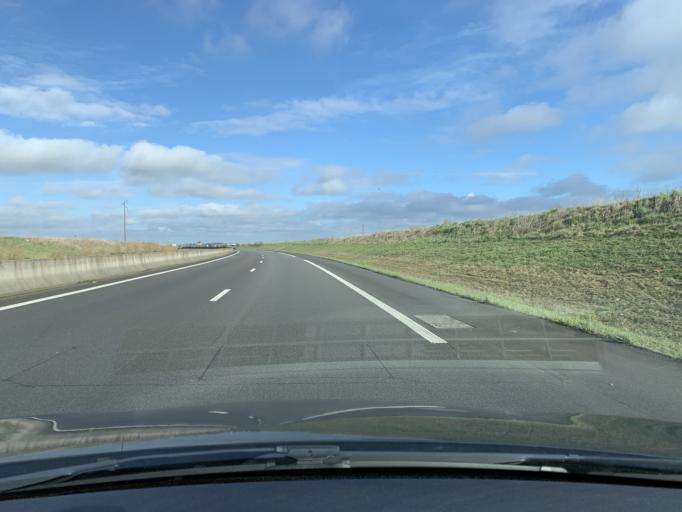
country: FR
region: Nord-Pas-de-Calais
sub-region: Departement du Nord
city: Cantin
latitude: 50.3101
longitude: 3.1364
